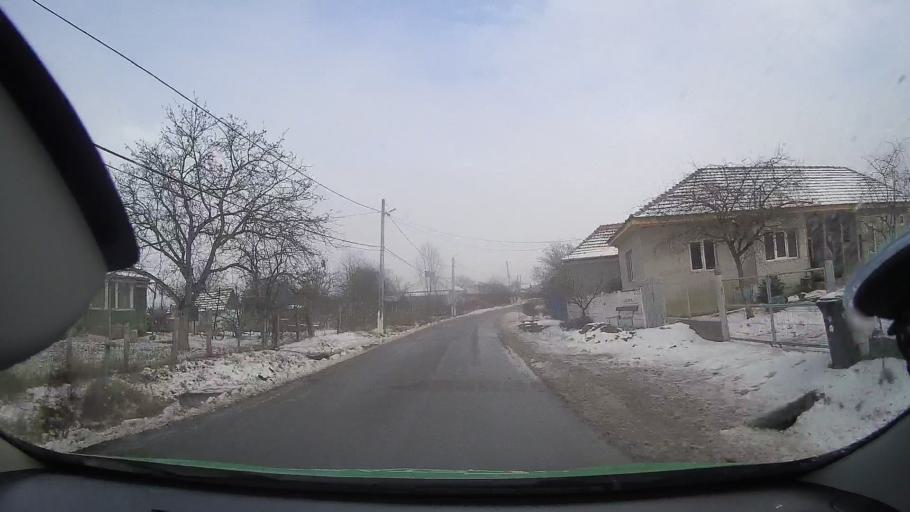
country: RO
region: Mures
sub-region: Comuna Chetani
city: Chetani
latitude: 46.4273
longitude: 23.9990
